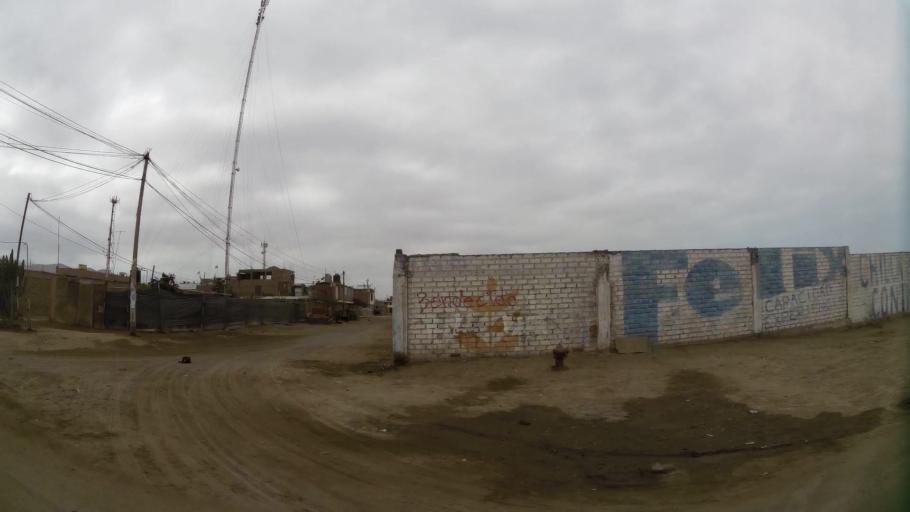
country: PE
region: Lima
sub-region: Provincia de Canete
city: Chilca
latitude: -12.5127
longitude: -76.7393
